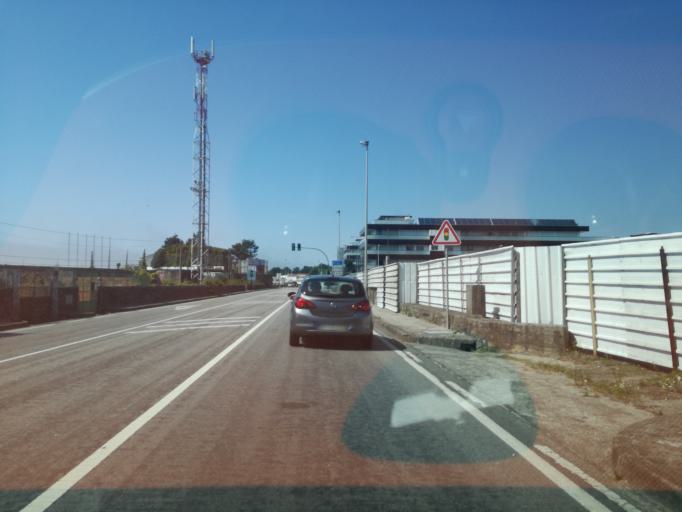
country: PT
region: Braga
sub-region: Esposende
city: Esposende
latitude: 41.5373
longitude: -8.7799
